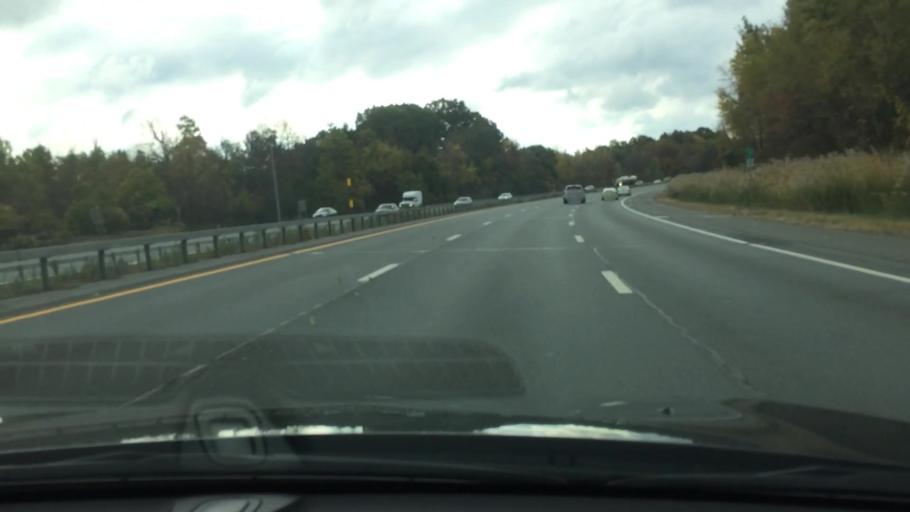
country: US
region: New York
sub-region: Albany County
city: Cohoes
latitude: 42.7878
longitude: -73.7584
